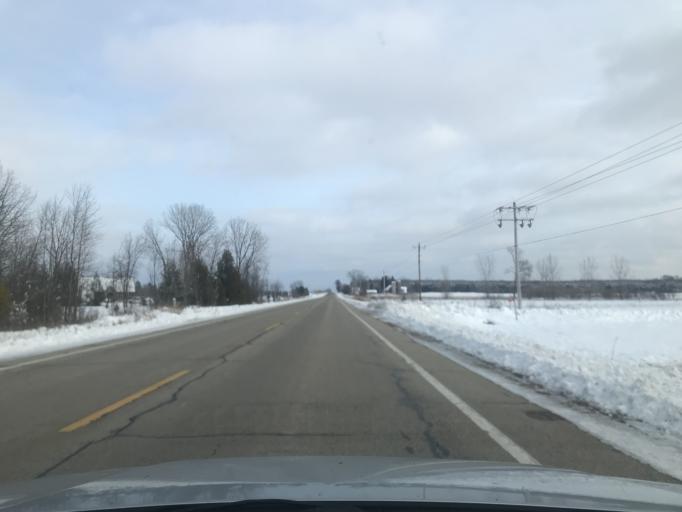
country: US
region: Wisconsin
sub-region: Oconto County
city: Oconto
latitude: 44.8927
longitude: -87.9556
